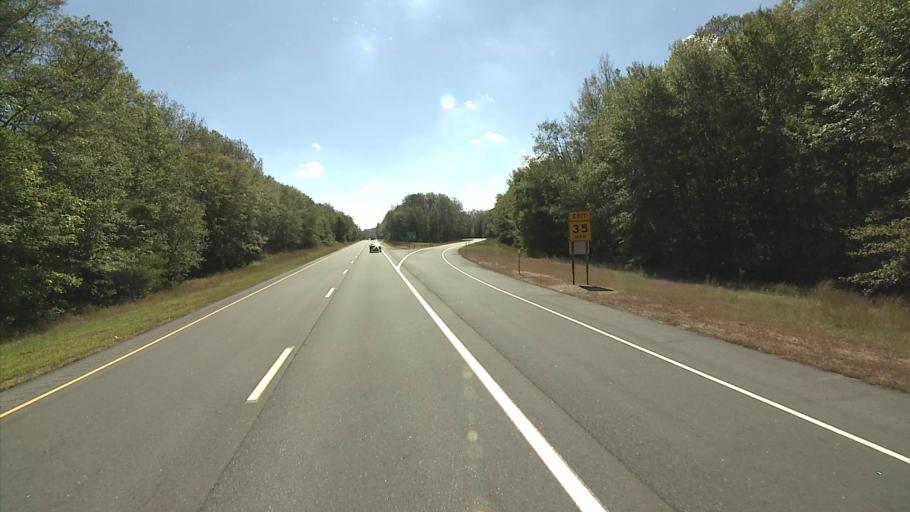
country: US
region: Connecticut
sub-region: New London County
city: Colchester
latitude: 41.5061
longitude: -72.3025
